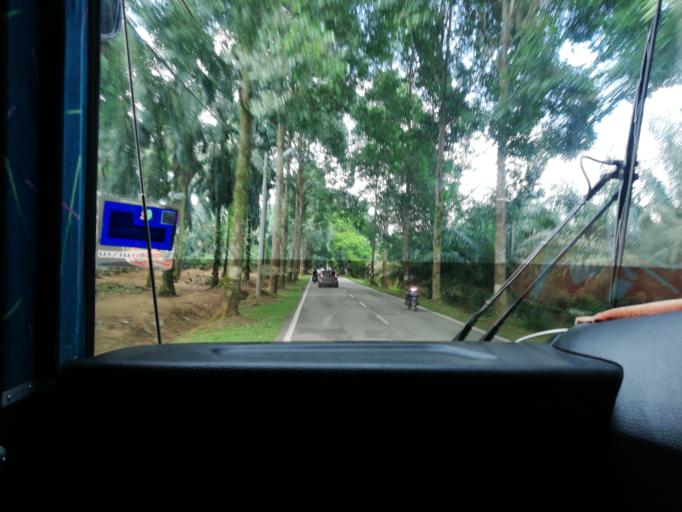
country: MY
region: Kedah
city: Kulim
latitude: 5.2447
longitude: 100.6021
